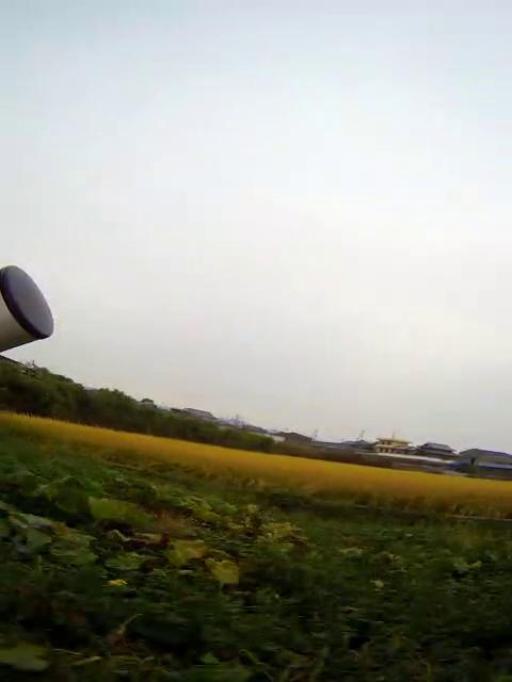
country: JP
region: Hyogo
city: Fukura
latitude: 34.3008
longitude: 134.7911
